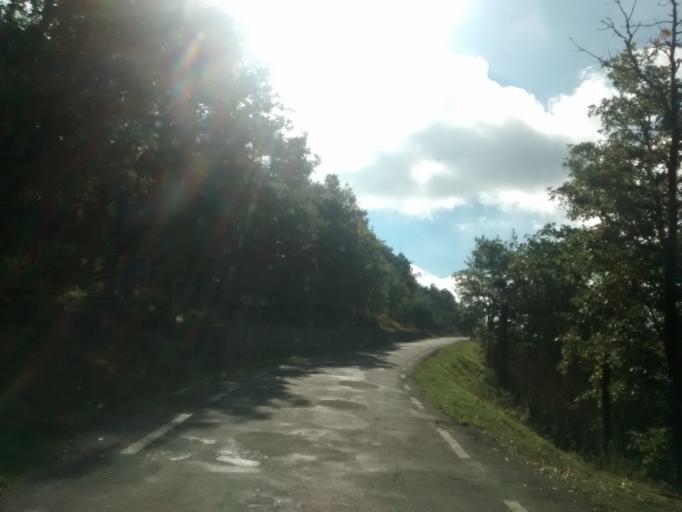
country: ES
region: Castille and Leon
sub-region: Provincia de Burgos
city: Arija
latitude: 42.9288
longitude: -4.0294
